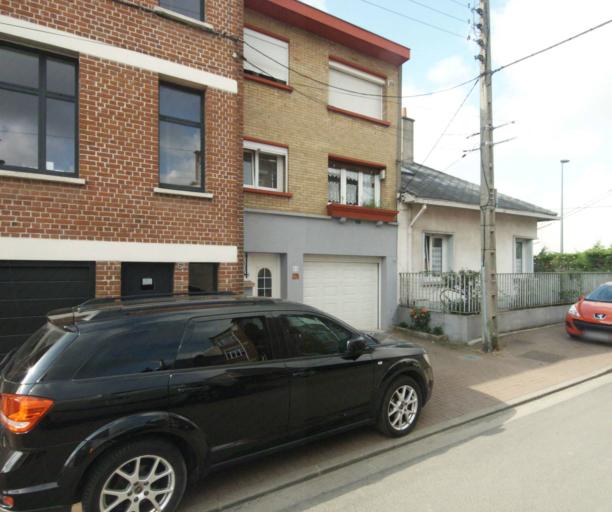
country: FR
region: Nord-Pas-de-Calais
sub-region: Departement du Nord
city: La Madeleine
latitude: 50.6488
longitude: 3.0931
